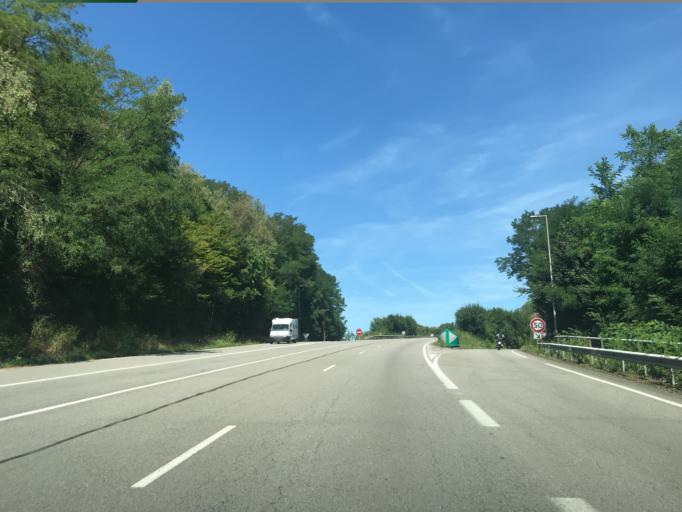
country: FR
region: Limousin
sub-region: Departement de la Correze
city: Tulle
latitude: 45.2716
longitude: 1.7894
